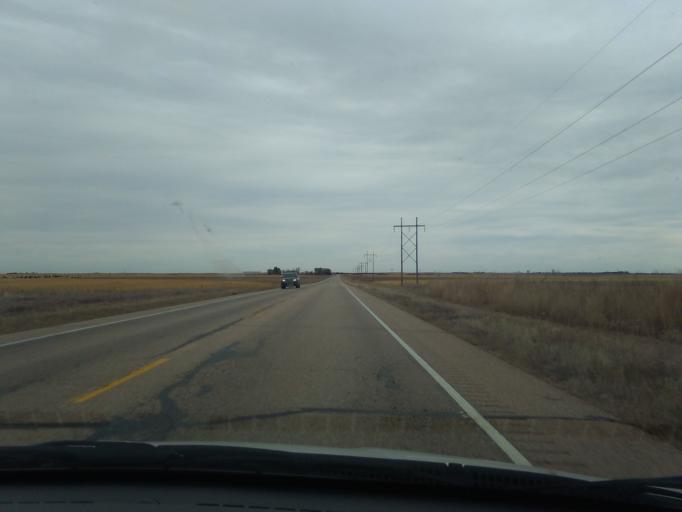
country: US
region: Colorado
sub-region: Yuma County
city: Yuma
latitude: 40.1474
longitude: -102.8050
